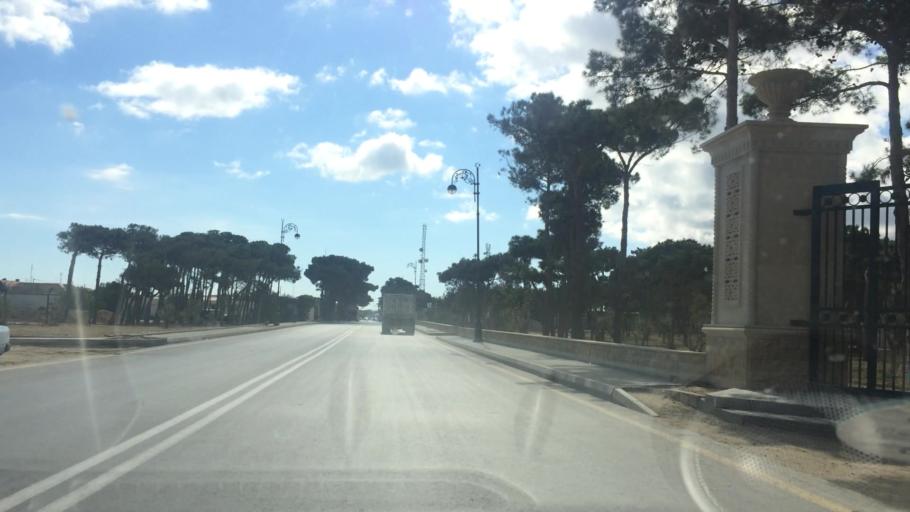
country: AZ
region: Baki
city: Pirallahi
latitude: 40.4666
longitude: 50.3272
